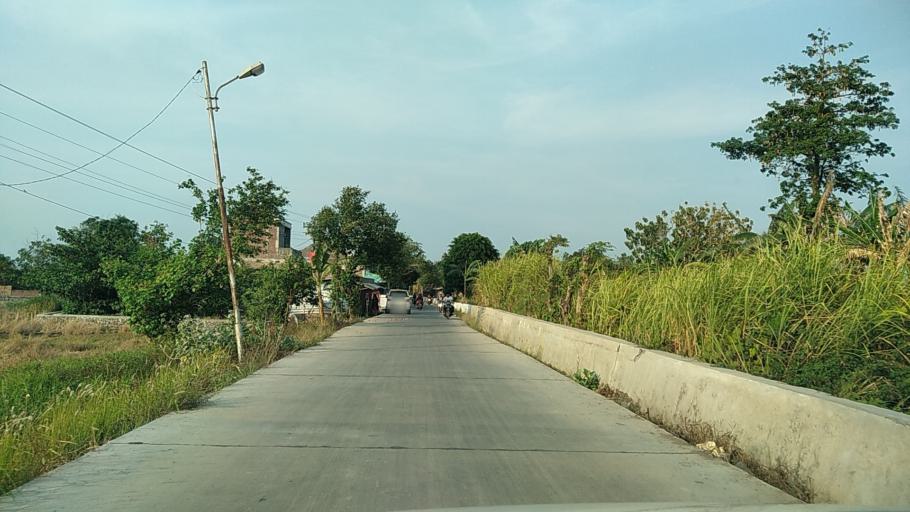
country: ID
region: Central Java
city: Semarang
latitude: -6.9567
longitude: 110.3044
